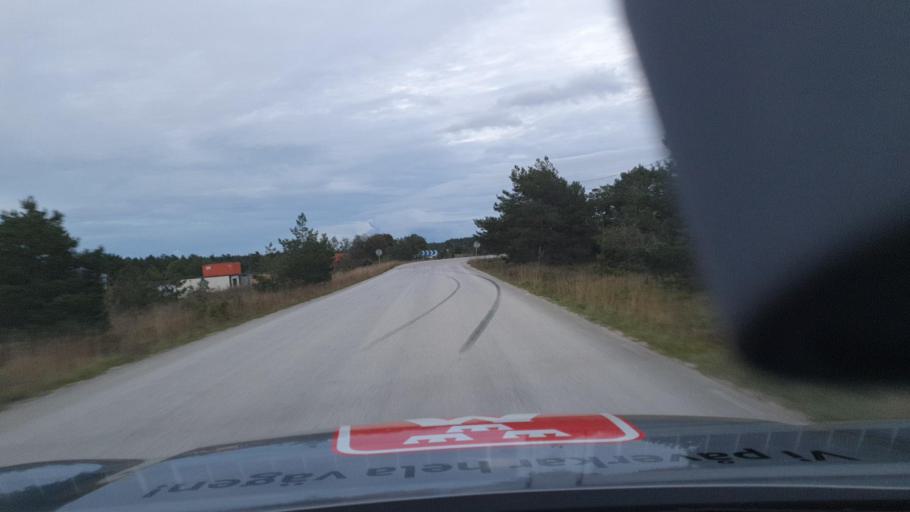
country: SE
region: Gotland
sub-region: Gotland
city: Visby
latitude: 57.6372
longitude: 18.3617
